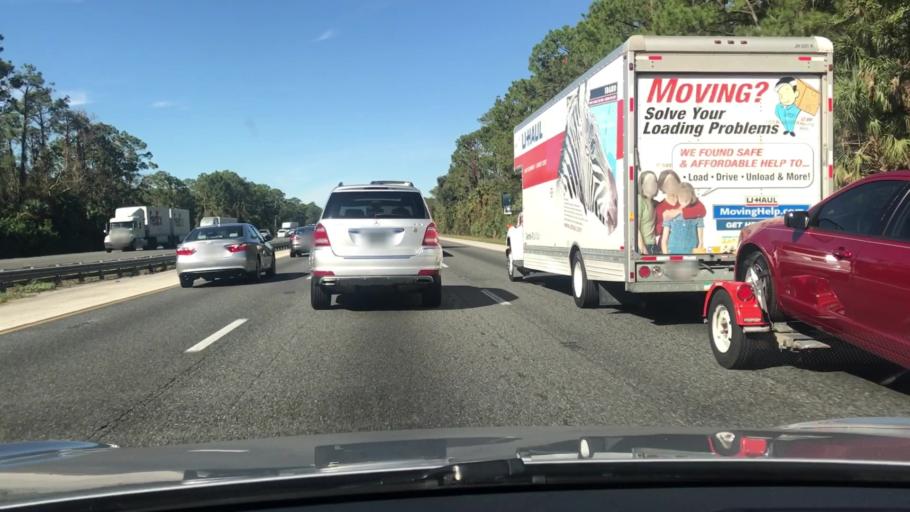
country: US
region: Florida
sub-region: Volusia County
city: Ormond-by-the-Sea
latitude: 29.3776
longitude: -81.1437
